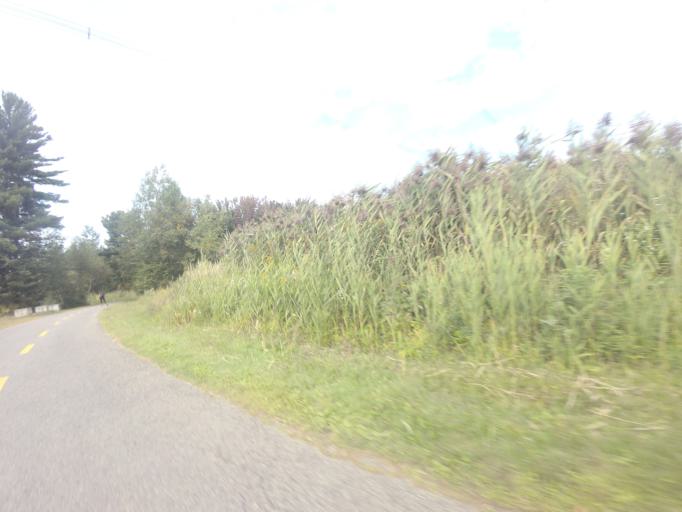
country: CA
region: Quebec
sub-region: Laurentides
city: Blainville
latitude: 45.6968
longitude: -73.8982
